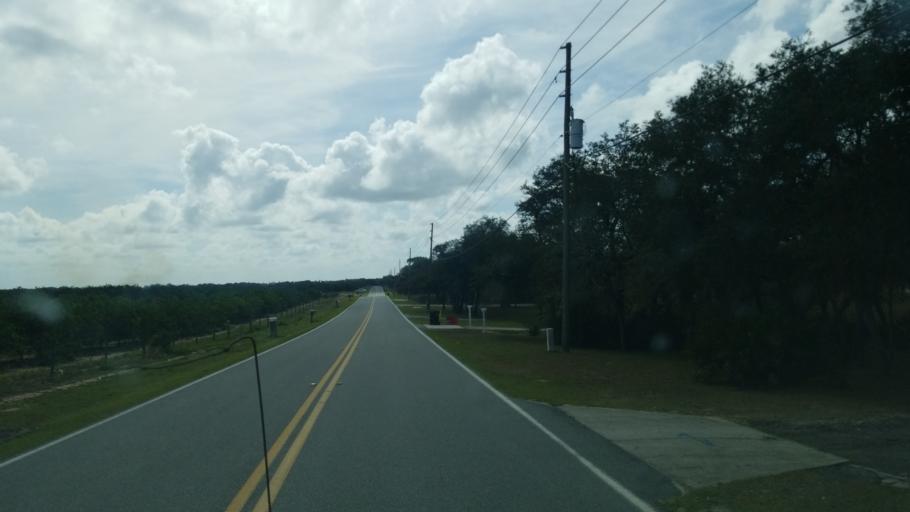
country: US
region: Florida
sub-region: Polk County
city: Dundee
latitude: 28.0301
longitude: -81.5292
